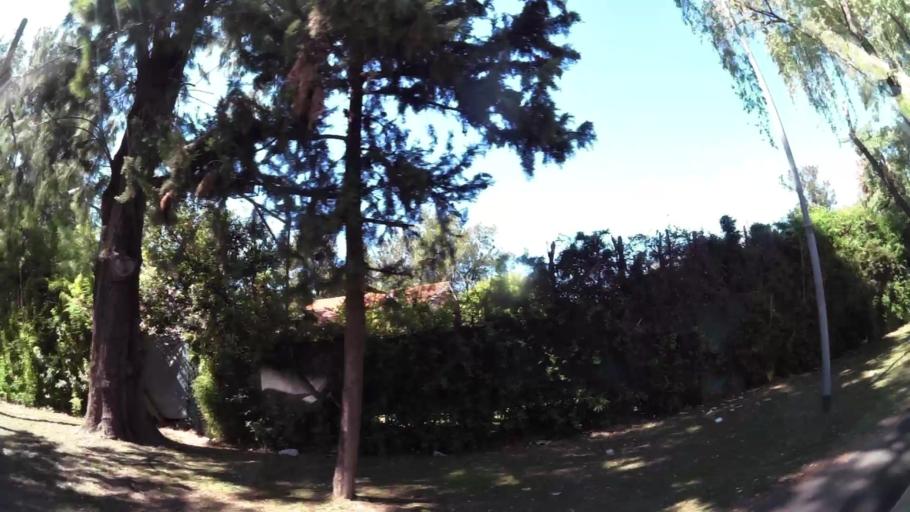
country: AR
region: Buenos Aires
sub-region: Partido de Tigre
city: Tigre
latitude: -34.5014
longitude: -58.6152
